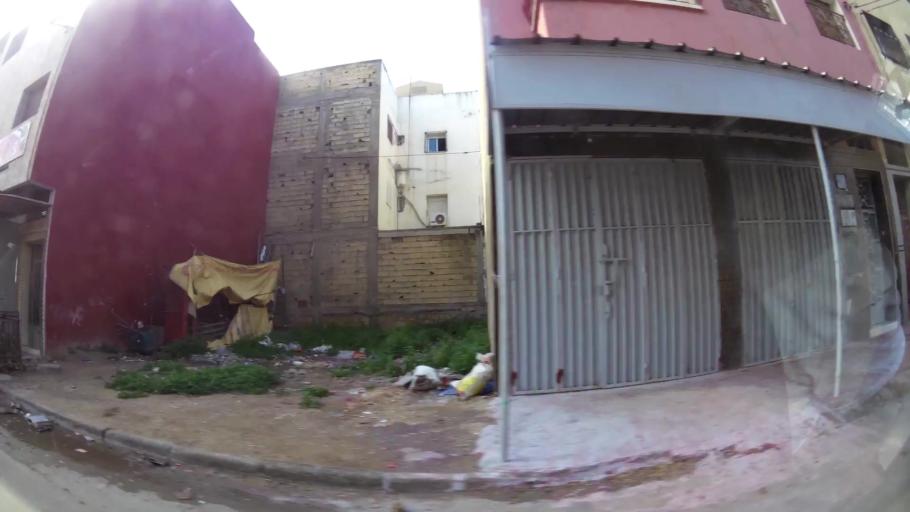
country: MA
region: Grand Casablanca
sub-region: Mediouna
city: Mediouna
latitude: 33.4566
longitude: -7.5166
